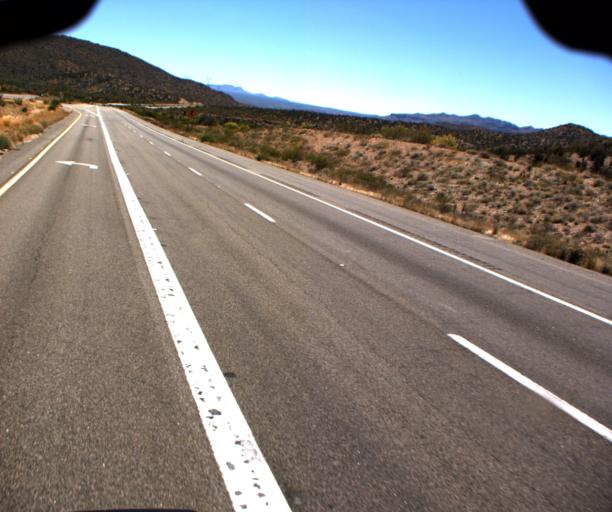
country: US
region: Arizona
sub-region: Yavapai County
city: Bagdad
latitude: 34.4287
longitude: -113.2483
